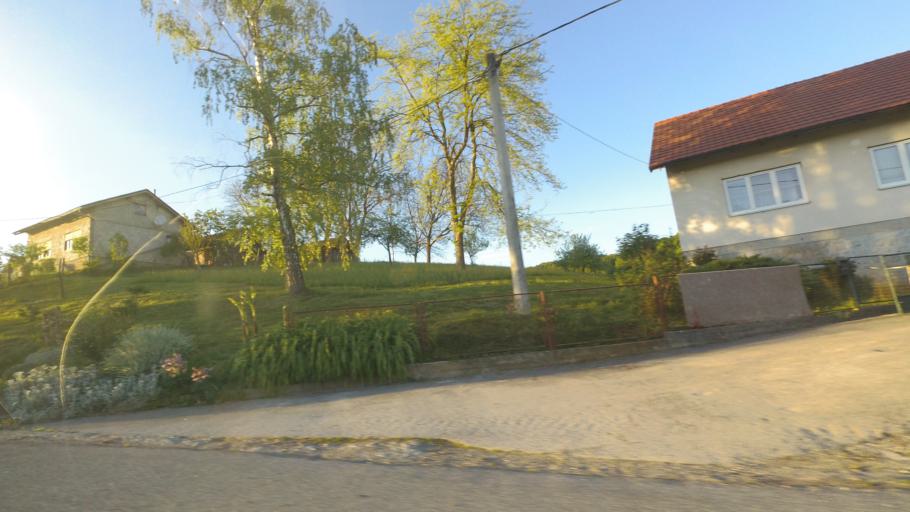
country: HR
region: Karlovacka
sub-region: Grad Karlovac
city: Karlovac
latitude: 45.4201
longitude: 15.5504
